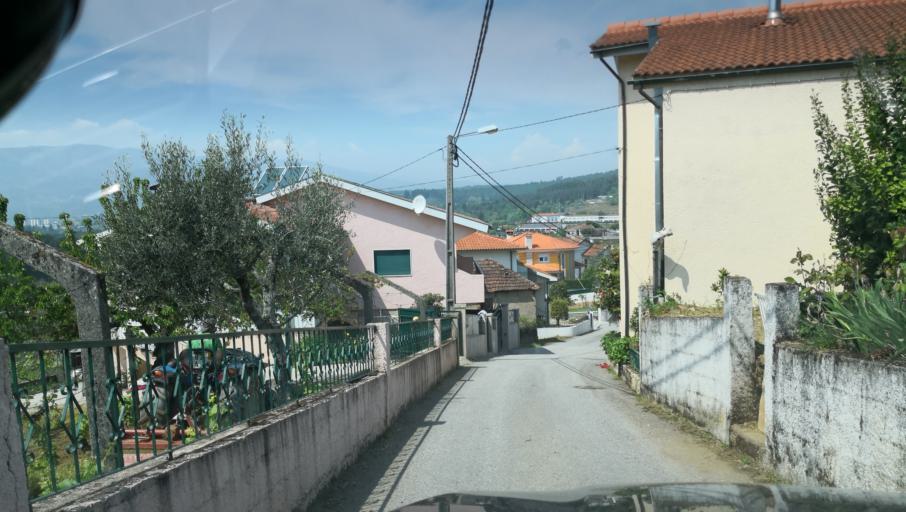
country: PT
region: Vila Real
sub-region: Vila Real
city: Vila Real
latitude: 41.2849
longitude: -7.7082
